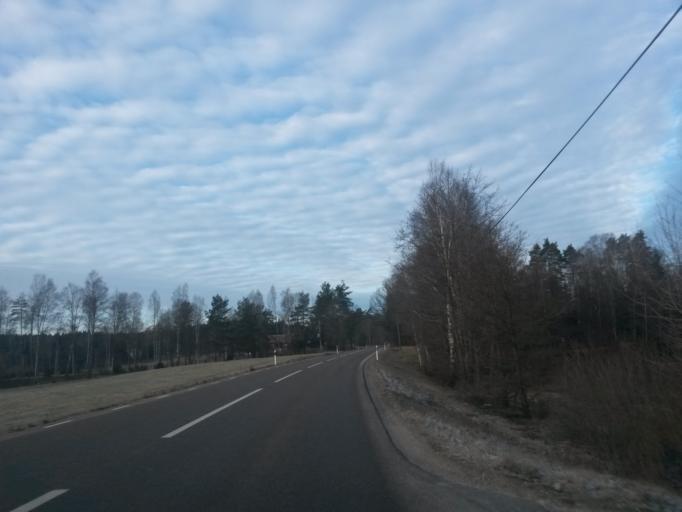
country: SE
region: Vaestra Goetaland
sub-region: Vargarda Kommun
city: Vargarda
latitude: 57.9116
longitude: 12.8999
